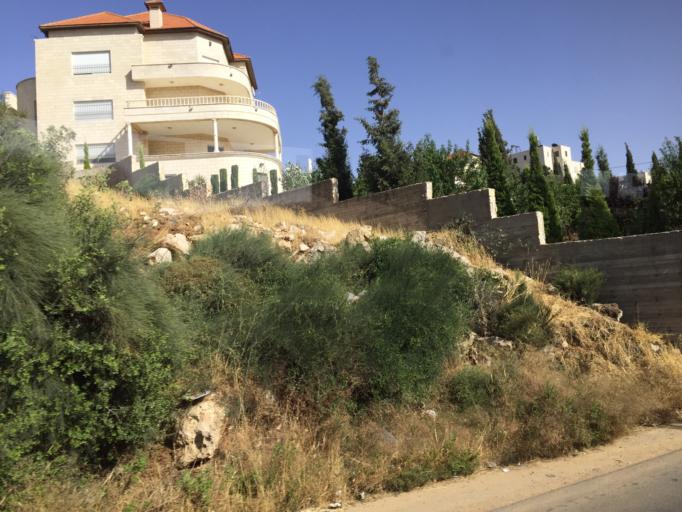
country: PS
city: Ad Dawhah
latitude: 31.7054
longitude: 35.1709
